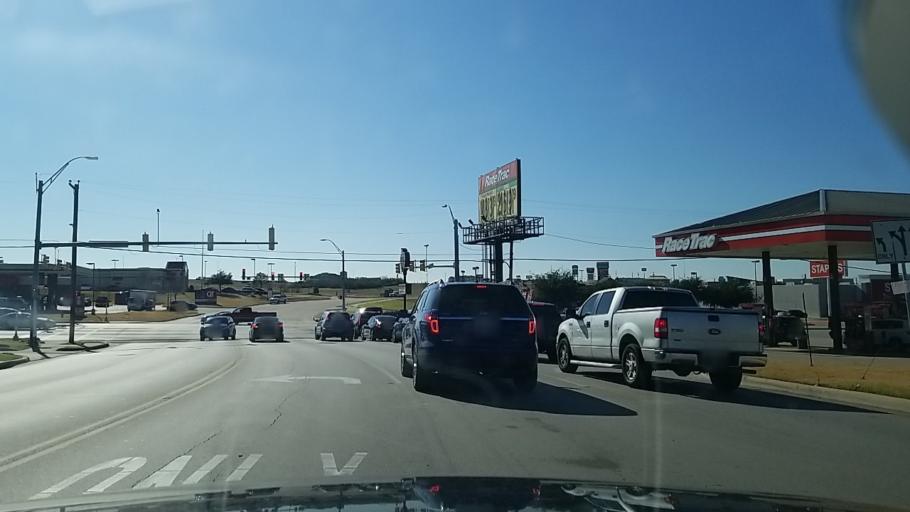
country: US
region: Texas
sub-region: Tarrant County
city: Sansom Park
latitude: 32.8104
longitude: -97.4216
